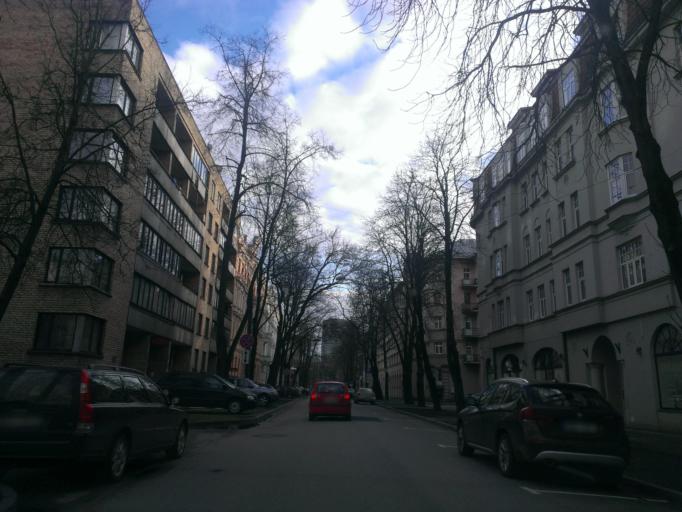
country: LV
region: Riga
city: Riga
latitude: 56.9611
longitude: 24.1002
